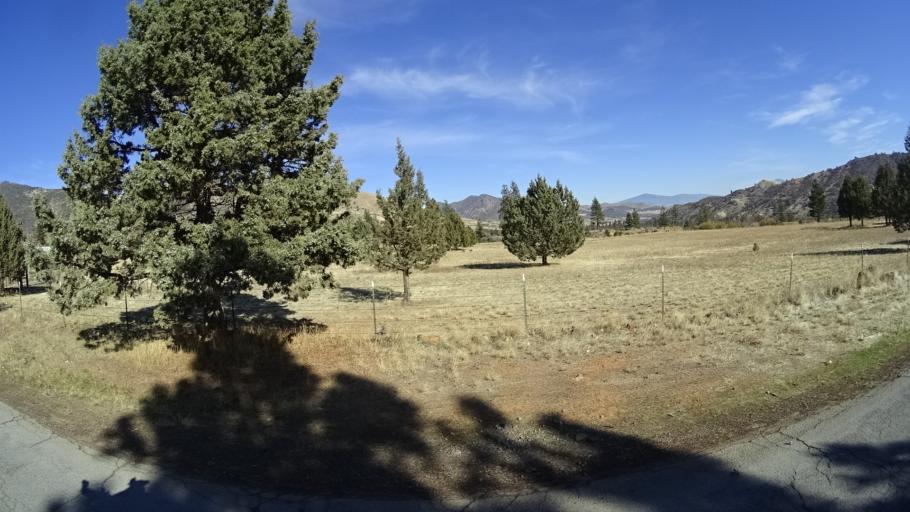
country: US
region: California
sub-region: Siskiyou County
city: Yreka
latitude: 41.7680
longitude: -122.6310
